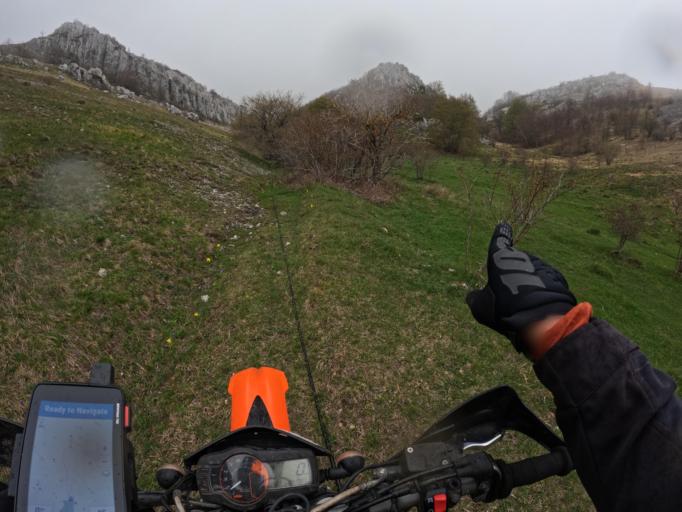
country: HR
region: Zadarska
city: Gracac
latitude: 44.4076
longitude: 15.9964
